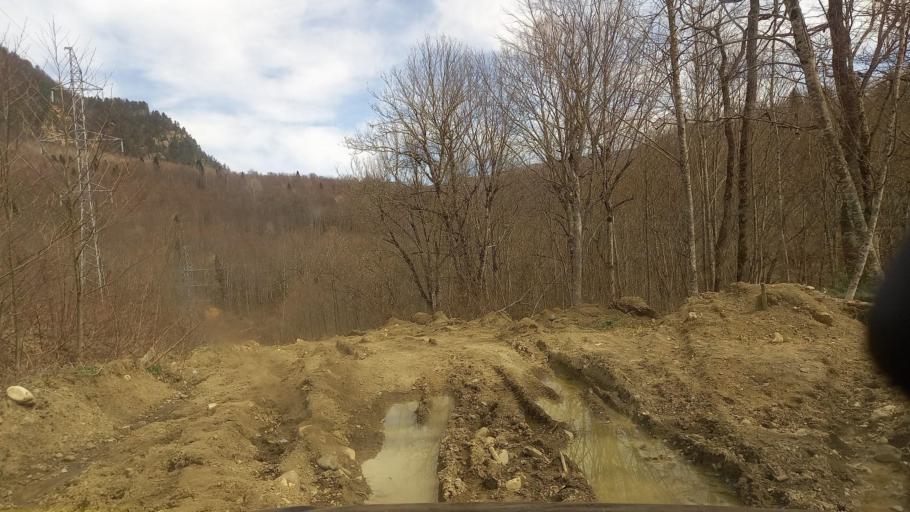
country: RU
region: Adygeya
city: Kamennomostskiy
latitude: 44.1081
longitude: 40.1029
